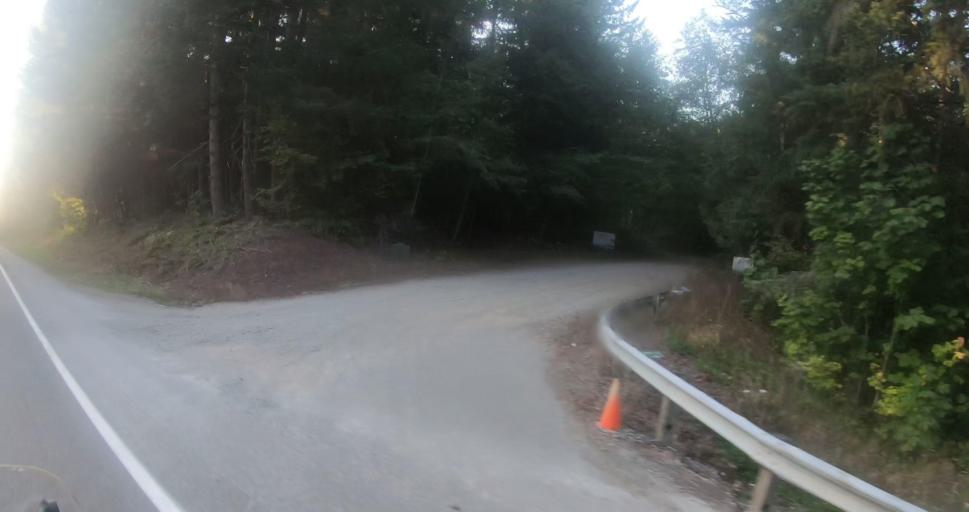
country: US
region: Washington
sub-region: Lewis County
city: Morton
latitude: 46.5382
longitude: -122.0231
